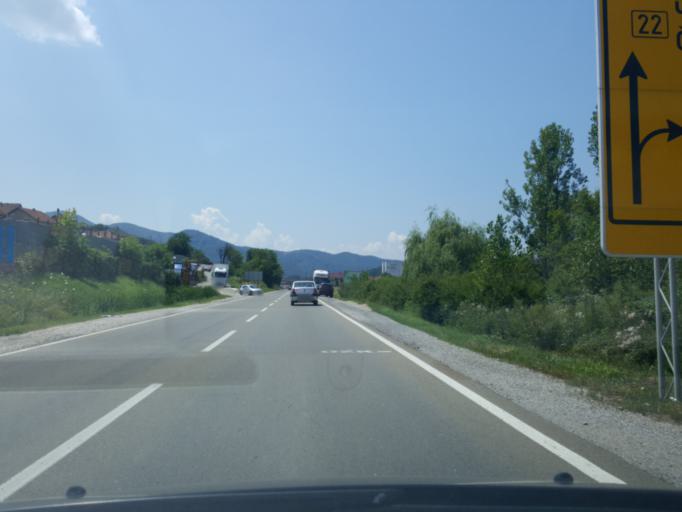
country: RS
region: Central Serbia
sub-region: Moravicki Okrug
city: Gornji Milanovac
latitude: 44.0253
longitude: 20.4683
